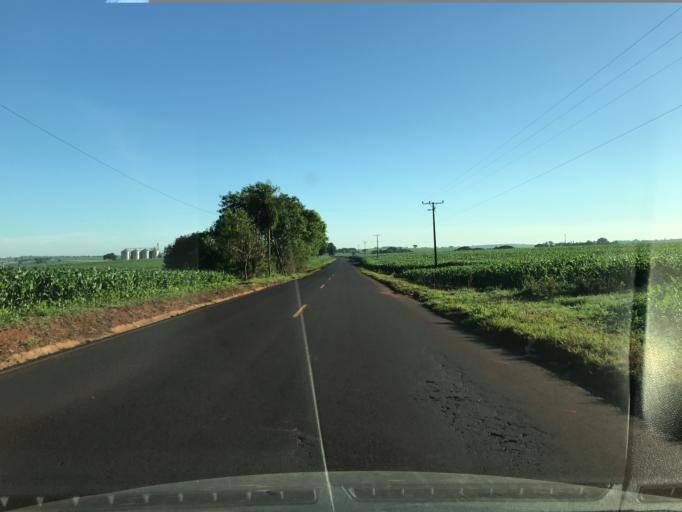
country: BR
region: Parana
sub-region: Palotina
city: Palotina
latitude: -24.1293
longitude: -53.8524
